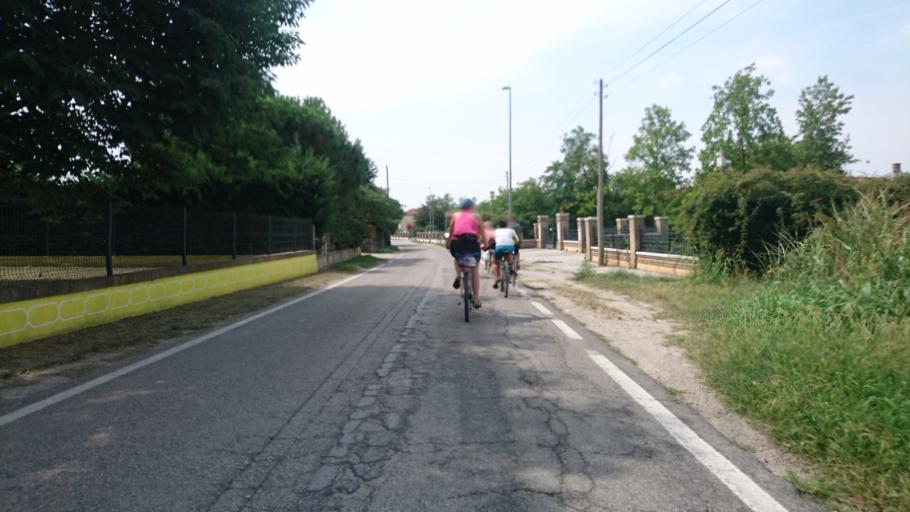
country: IT
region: Veneto
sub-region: Provincia di Rovigo
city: Rosolina
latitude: 45.0842
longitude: 12.2336
